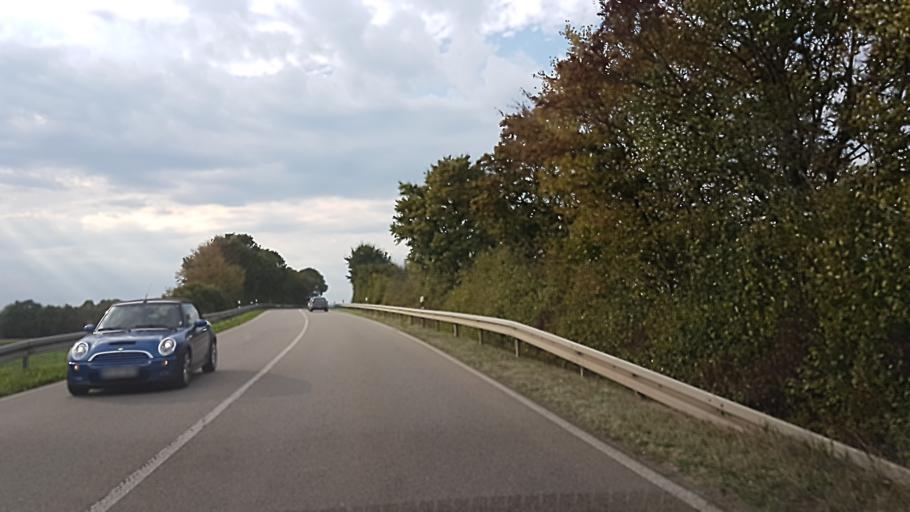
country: DE
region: Baden-Wuerttemberg
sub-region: Freiburg Region
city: Sexau
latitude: 48.0956
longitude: 7.8910
